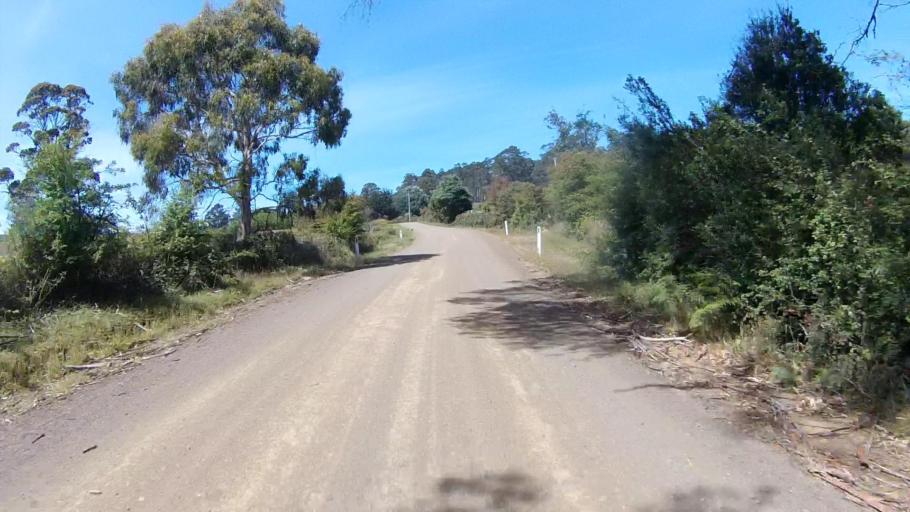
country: AU
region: Tasmania
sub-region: Sorell
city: Sorell
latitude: -42.7032
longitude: 147.7428
